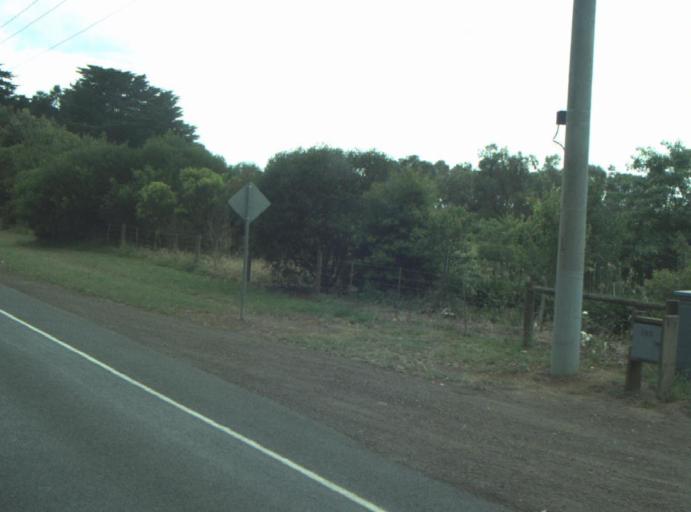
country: AU
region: Victoria
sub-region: Greater Geelong
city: Leopold
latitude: -38.2377
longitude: 144.5018
